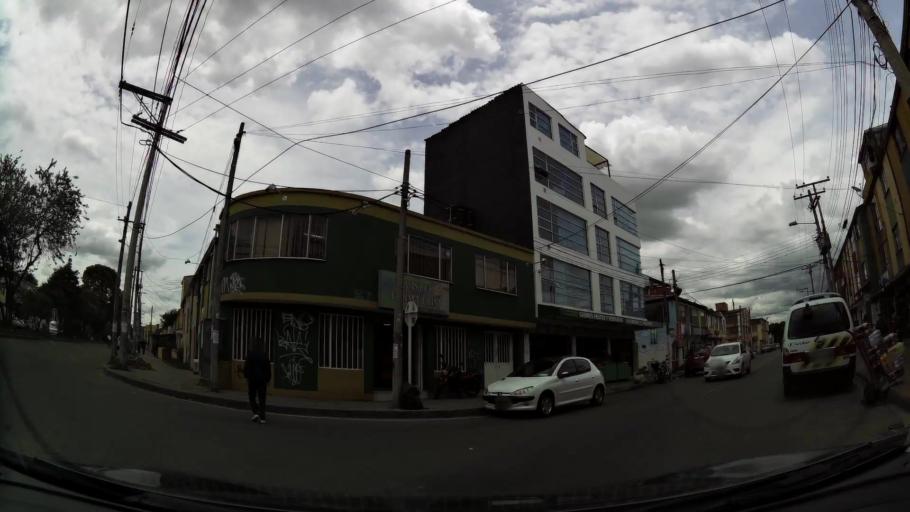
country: CO
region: Cundinamarca
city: Funza
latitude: 4.7159
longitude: -74.1209
